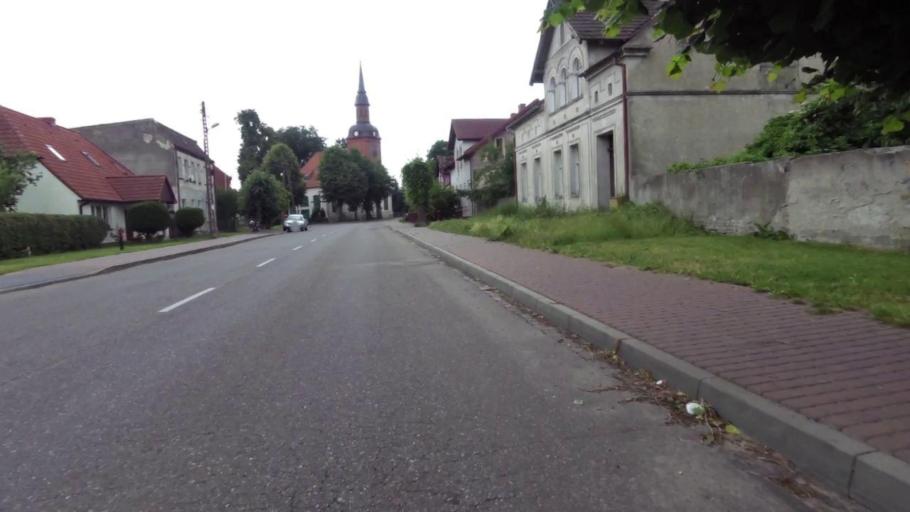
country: PL
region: West Pomeranian Voivodeship
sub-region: Powiat goleniowski
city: Stepnica
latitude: 53.6542
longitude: 14.6215
